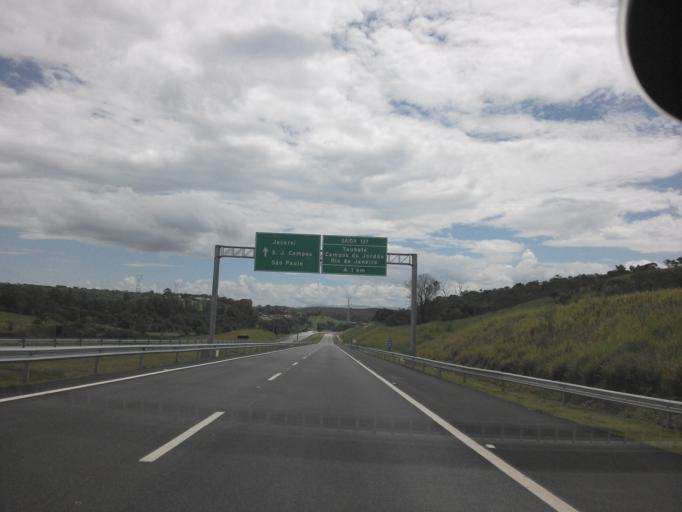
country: BR
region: Sao Paulo
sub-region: Taubate
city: Taubate
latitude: -23.1024
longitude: -45.5928
